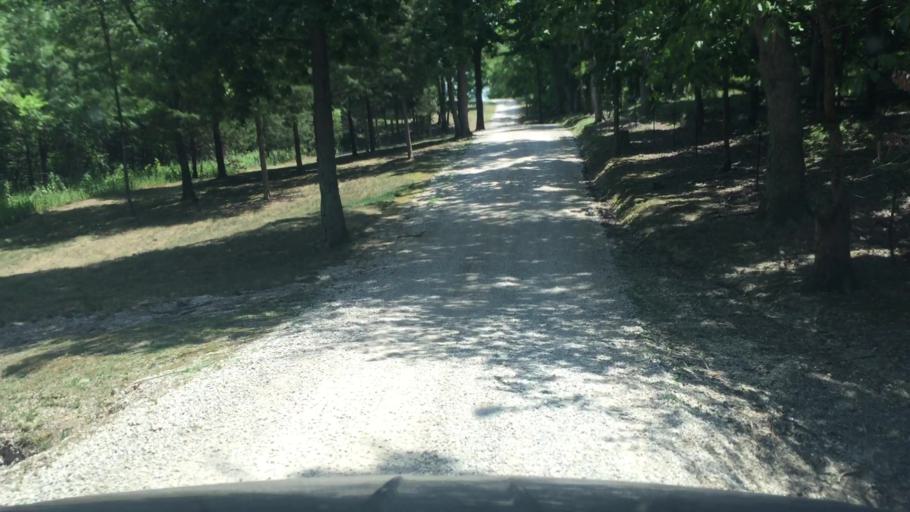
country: US
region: Missouri
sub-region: Miller County
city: Tuscumbia
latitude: 38.1310
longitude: -92.4400
